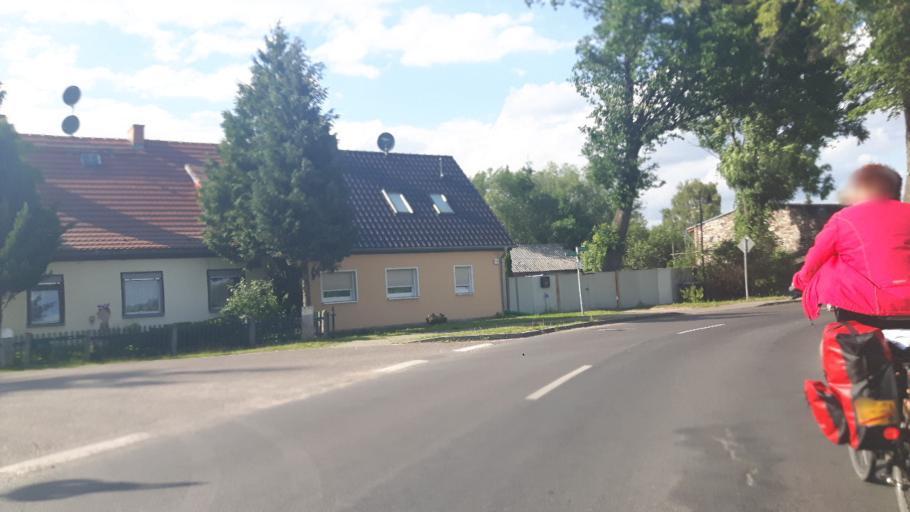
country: DE
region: Brandenburg
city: Melchow
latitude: 52.7369
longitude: 13.7106
